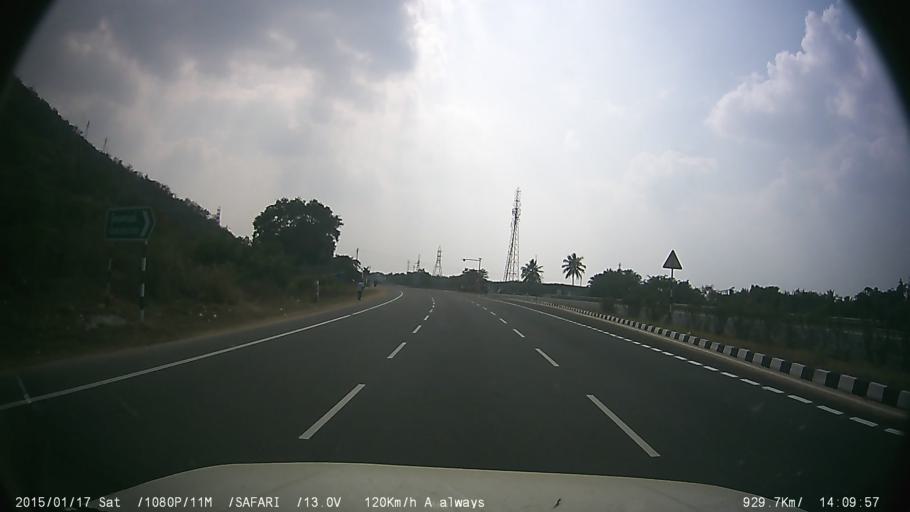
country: IN
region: Tamil Nadu
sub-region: Vellore
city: Ambur
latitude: 12.8121
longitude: 78.7432
